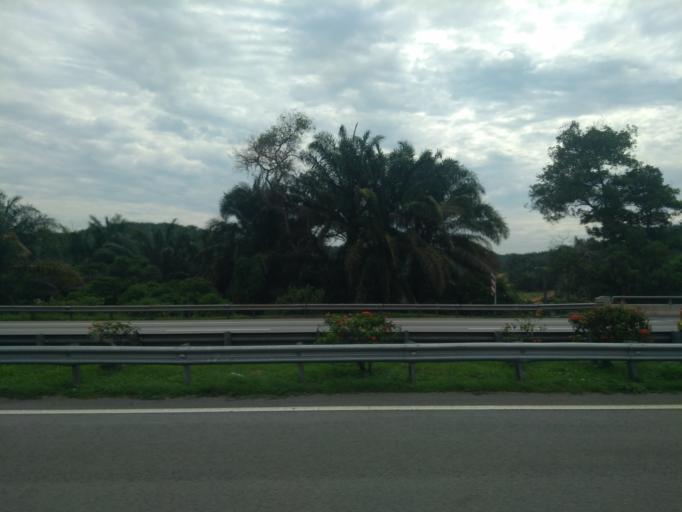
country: MY
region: Negeri Sembilan
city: Seremban
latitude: 2.6507
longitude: 101.9914
